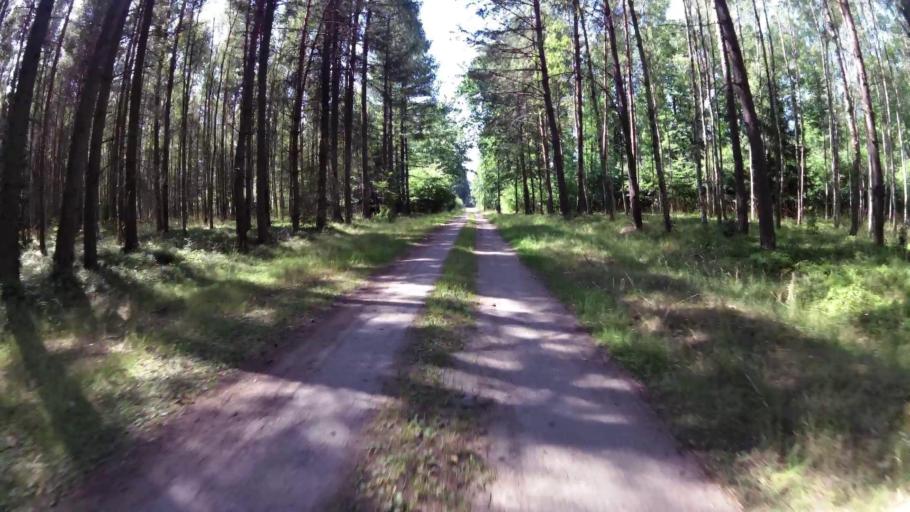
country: PL
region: West Pomeranian Voivodeship
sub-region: Powiat drawski
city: Czaplinek
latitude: 53.4040
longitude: 16.2488
